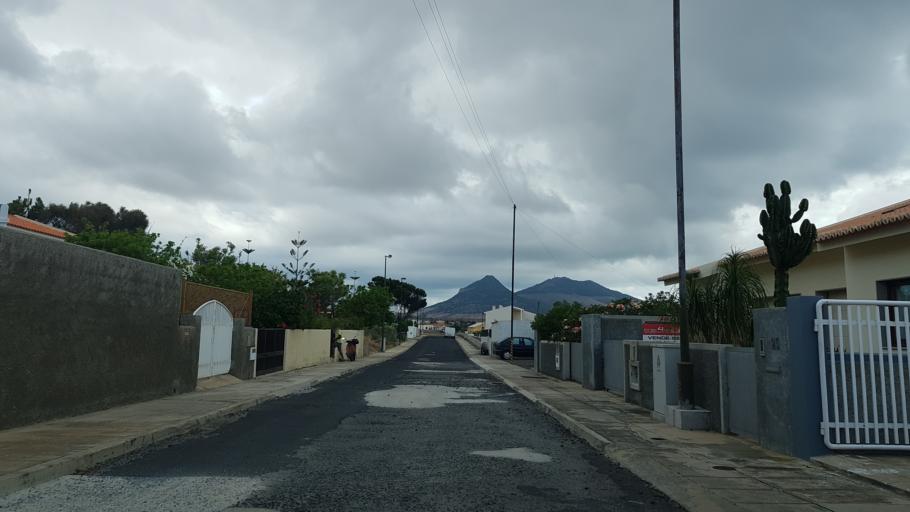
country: PT
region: Madeira
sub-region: Porto Santo
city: Vila de Porto Santo
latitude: 33.0400
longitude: -16.3617
